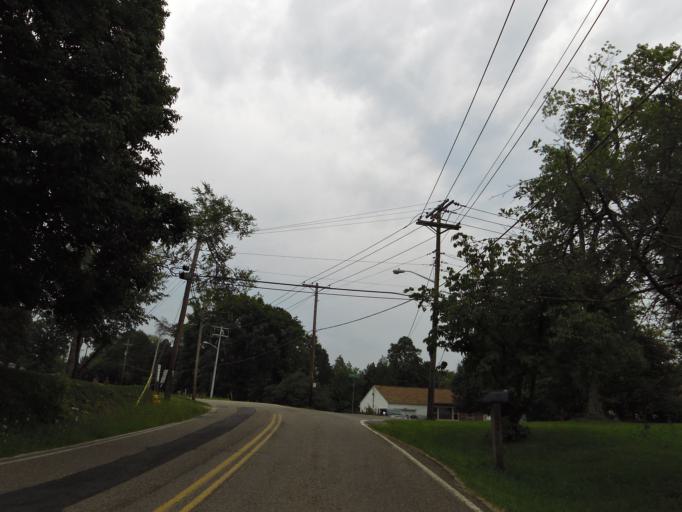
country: US
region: Tennessee
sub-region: Knox County
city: Knoxville
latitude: 35.9269
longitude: -83.8679
